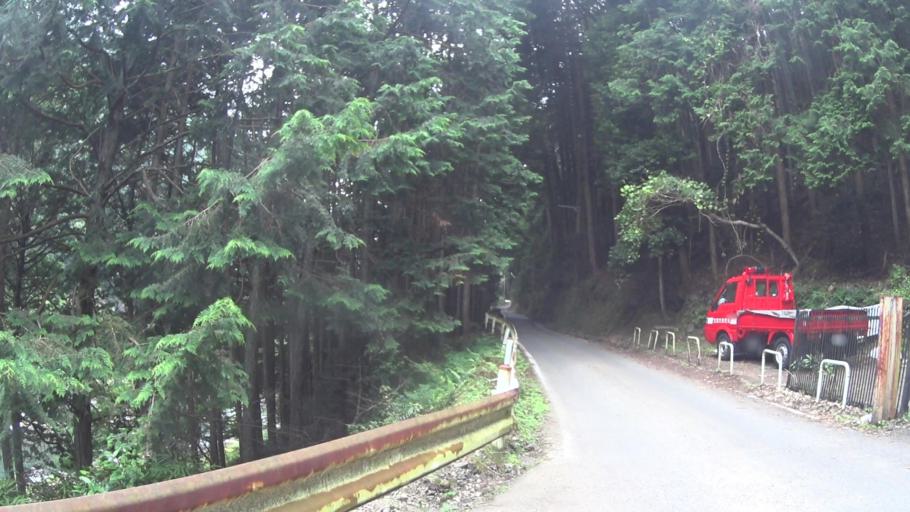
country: JP
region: Kyoto
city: Kameoka
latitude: 35.0270
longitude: 135.6453
